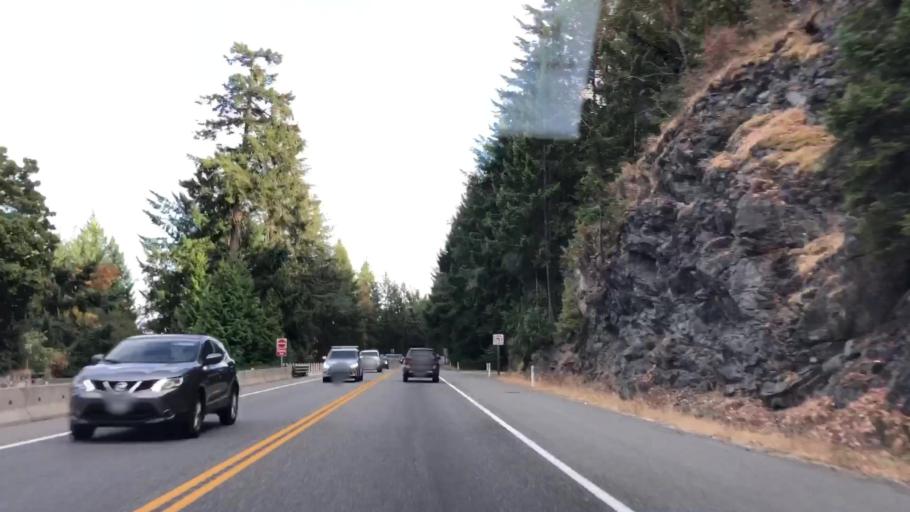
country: CA
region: British Columbia
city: Langford
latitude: 48.5784
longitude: -123.5291
